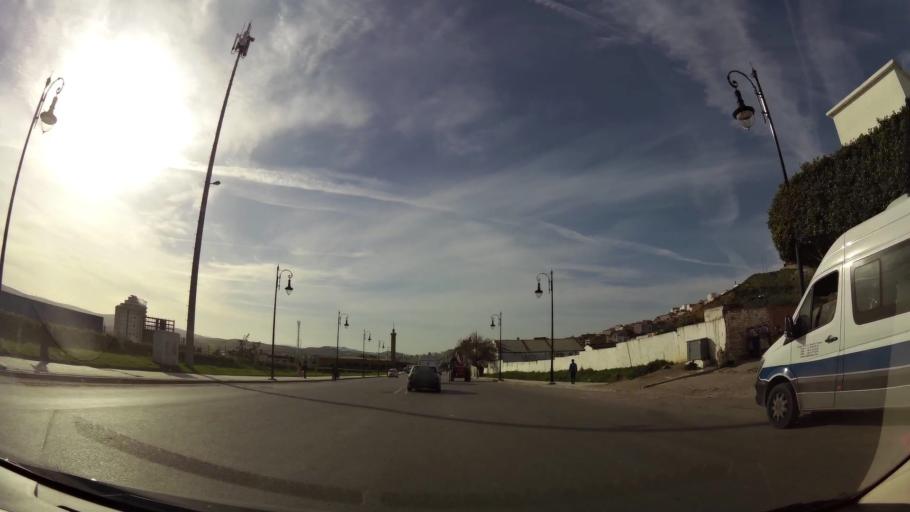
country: MA
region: Tanger-Tetouan
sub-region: Tanger-Assilah
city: Tangier
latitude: 35.7668
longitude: -5.7847
